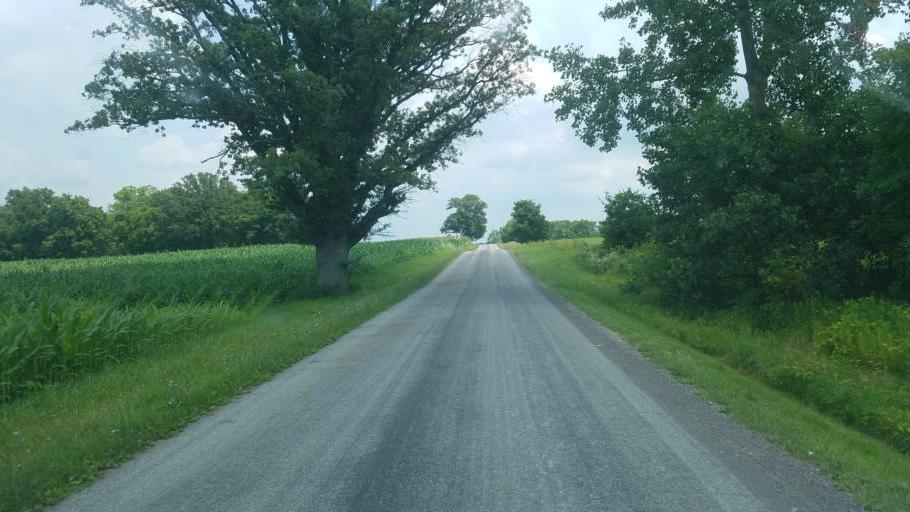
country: US
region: Ohio
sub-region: Hardin County
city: Kenton
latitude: 40.5919
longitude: -83.6395
